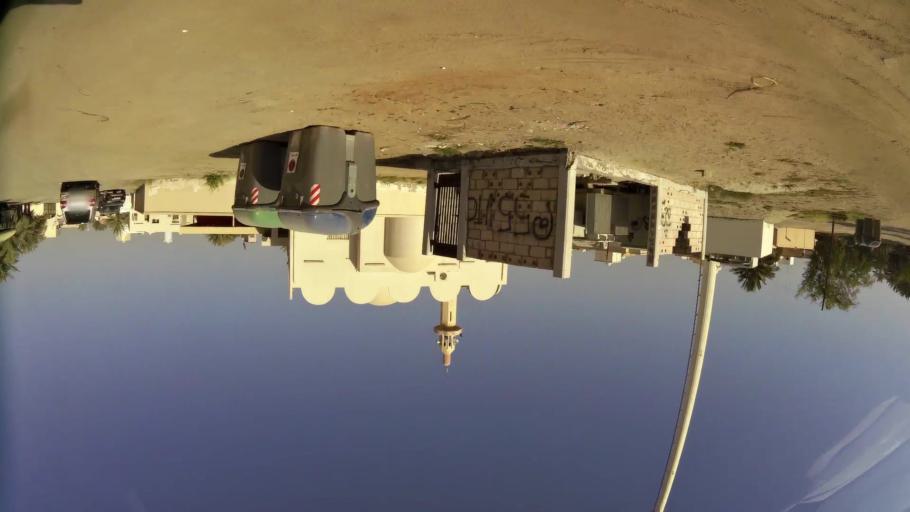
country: AE
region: Ajman
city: Ajman
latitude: 25.4018
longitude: 55.4626
